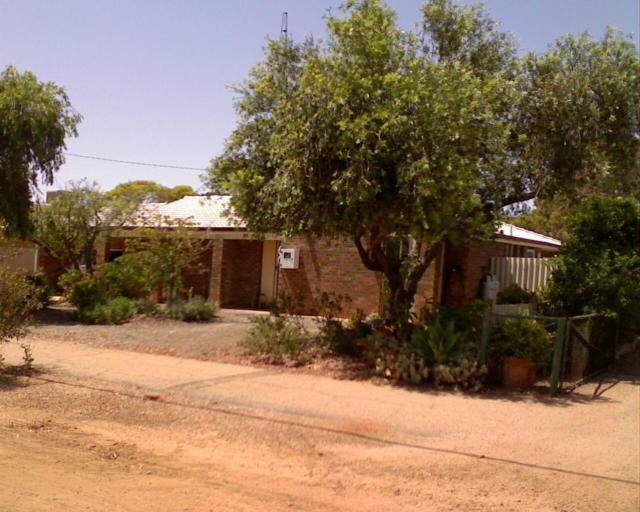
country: AU
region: Western Australia
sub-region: Merredin
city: Merredin
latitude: -30.9179
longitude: 118.2073
